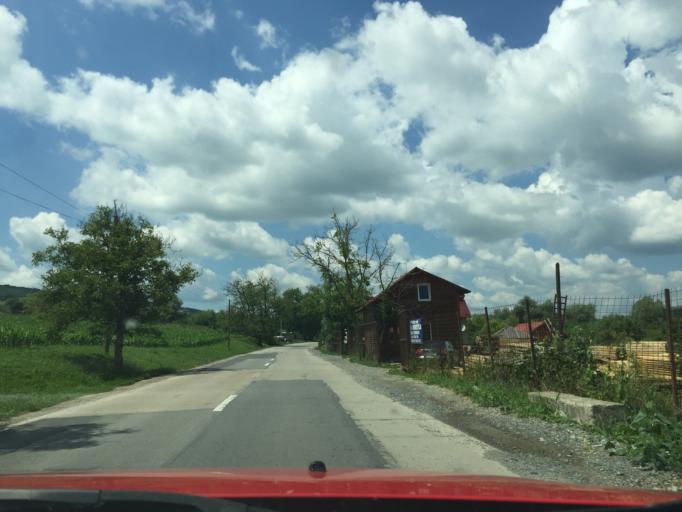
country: RO
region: Cluj
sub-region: Comuna Chinteni
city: Chinteni
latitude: 46.8337
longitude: 23.5749
